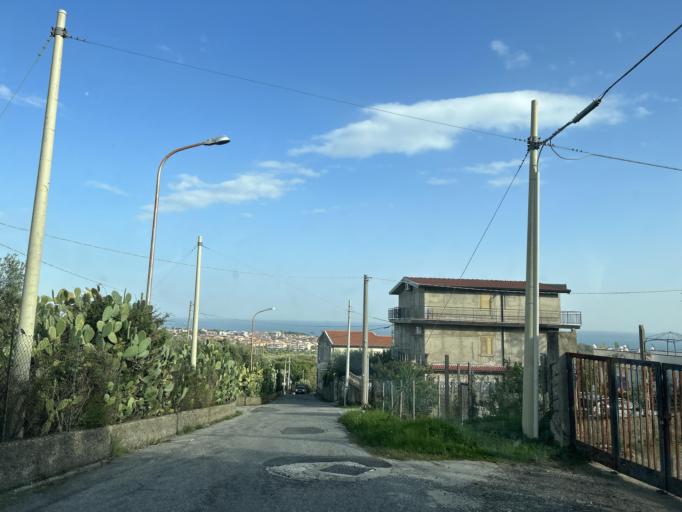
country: IT
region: Calabria
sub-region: Provincia di Catanzaro
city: Montepaone
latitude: 38.7162
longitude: 16.5185
